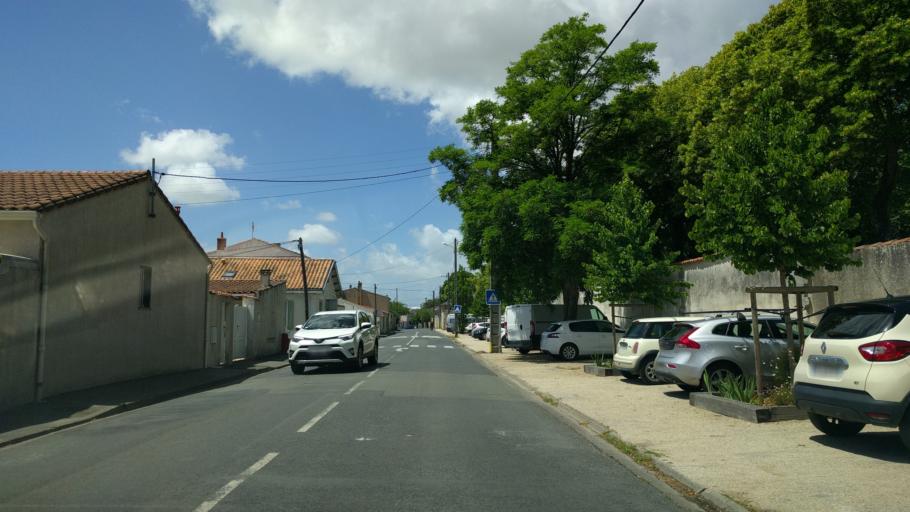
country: FR
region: Poitou-Charentes
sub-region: Departement de la Charente-Maritime
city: La Rochelle
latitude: 46.1629
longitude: -1.1321
